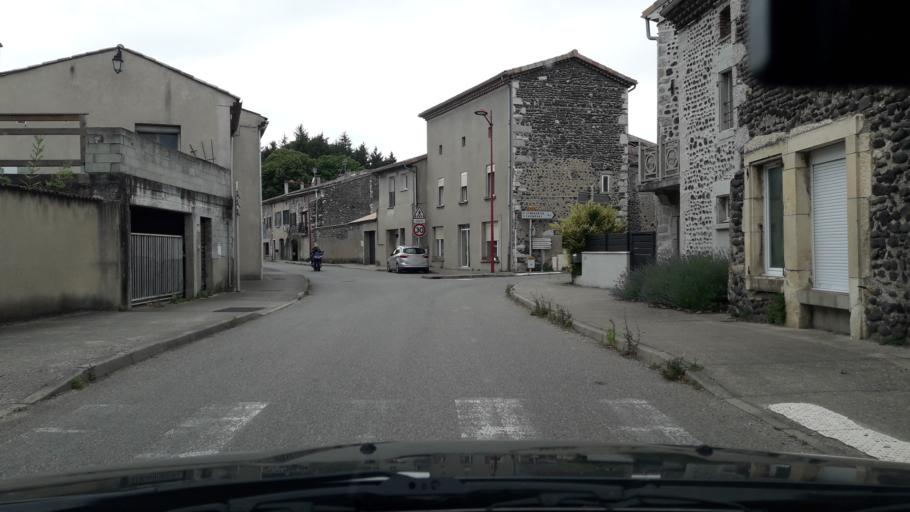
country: FR
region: Rhone-Alpes
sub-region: Departement de l'Ardeche
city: Saint-Julien-en-Saint-Alban
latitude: 44.7131
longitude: 4.7084
